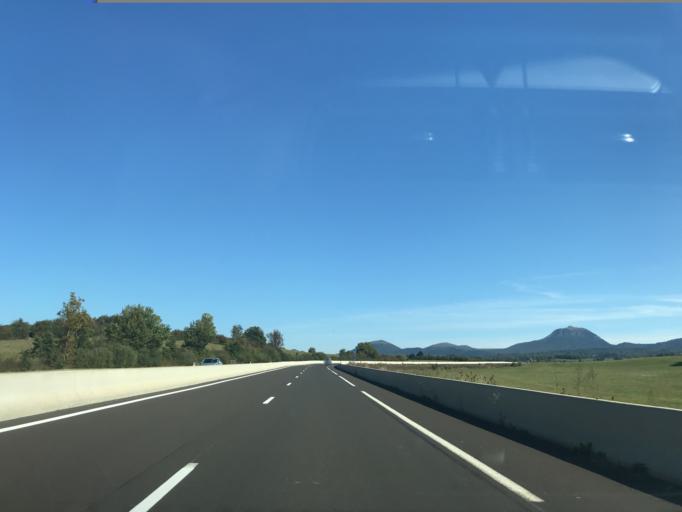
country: FR
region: Auvergne
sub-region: Departement du Puy-de-Dome
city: Gelles
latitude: 45.7363
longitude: 2.8420
